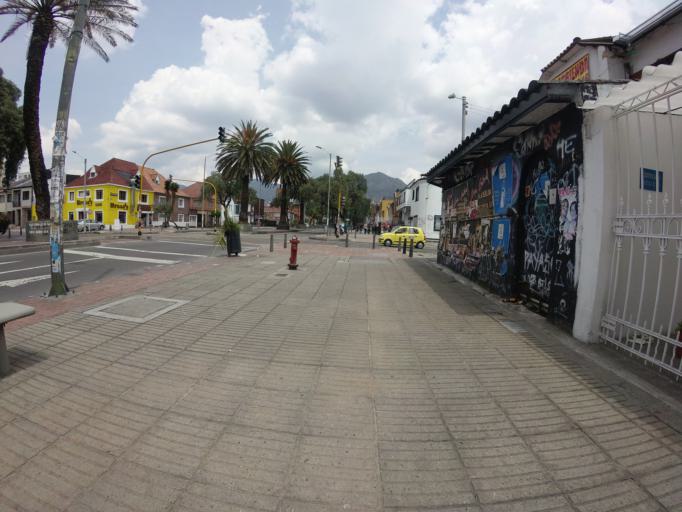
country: CO
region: Bogota D.C.
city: Bogota
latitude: 4.6448
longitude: -74.0708
